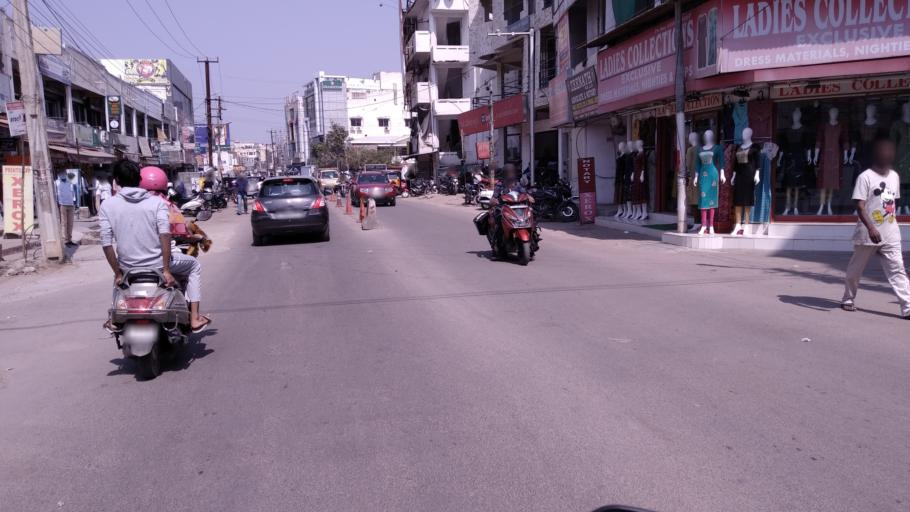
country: IN
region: Telangana
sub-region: Rangareddi
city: Quthbullapur
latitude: 17.4641
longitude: 78.4836
